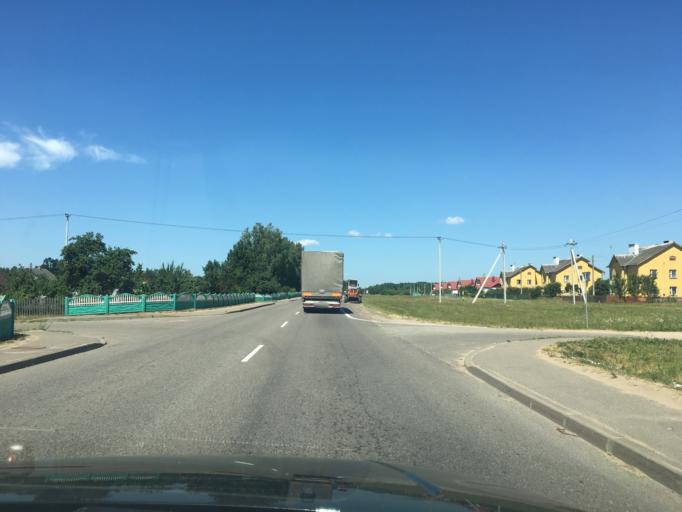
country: BY
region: Grodnenskaya
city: Iwye
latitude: 54.0357
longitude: 25.9215
